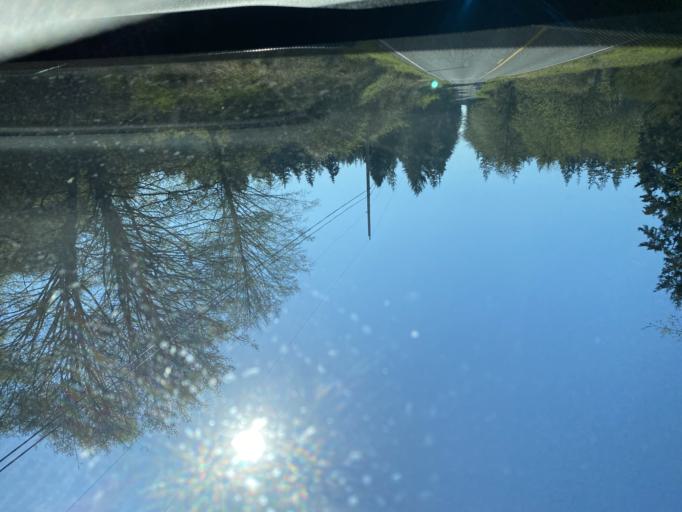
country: US
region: Washington
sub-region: Island County
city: Freeland
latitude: 48.0873
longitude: -122.5822
